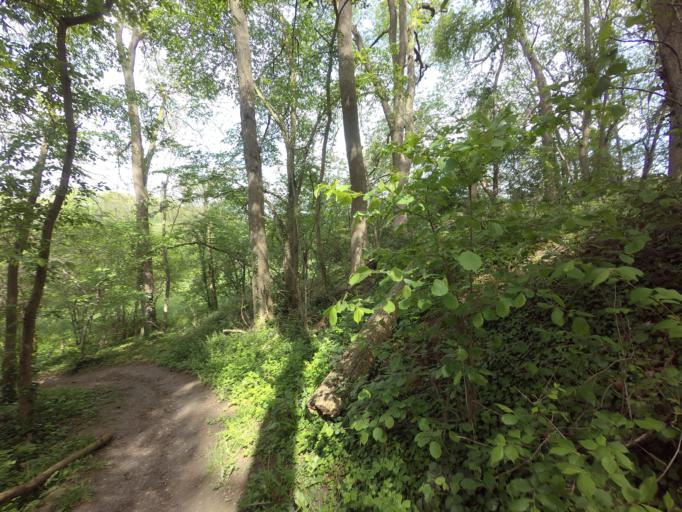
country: NL
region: Limburg
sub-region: Valkenburg aan de Geul
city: Berg
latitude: 50.8378
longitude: 5.7721
